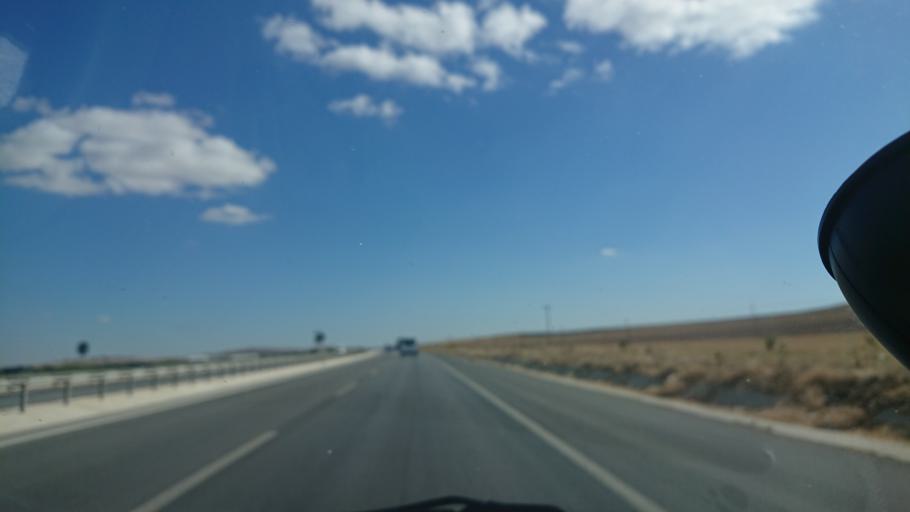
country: TR
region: Eskisehir
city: Mahmudiye
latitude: 39.5307
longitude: 30.9486
